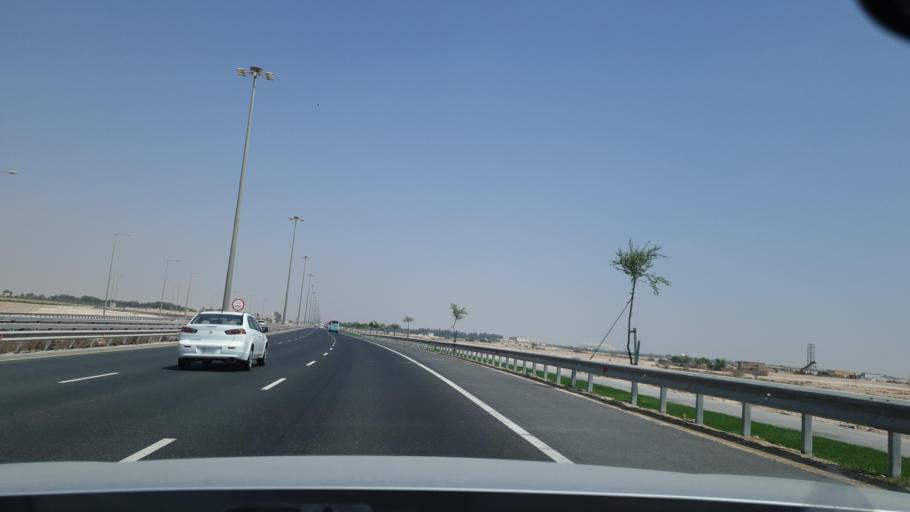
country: QA
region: Baladiyat az Za`ayin
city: Az Za`ayin
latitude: 25.6239
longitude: 51.4142
